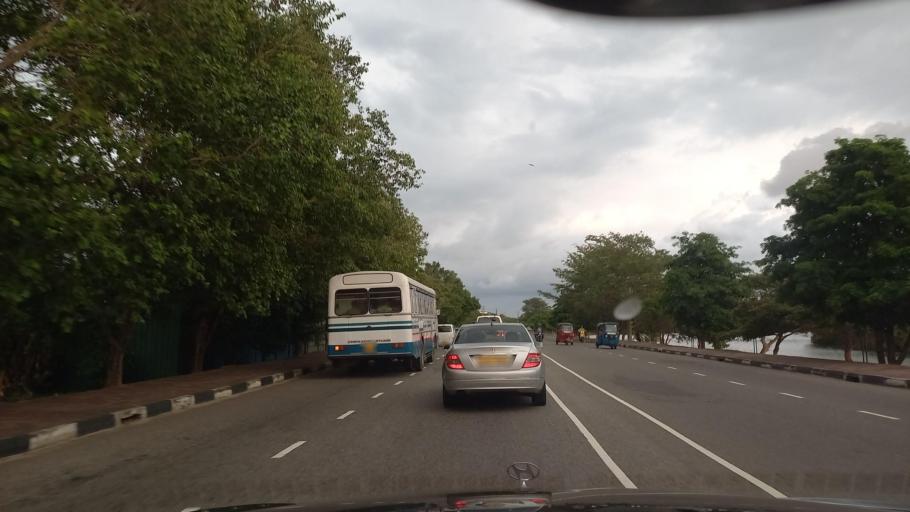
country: LK
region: Western
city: Battaramulla South
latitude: 6.8846
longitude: 79.9251
